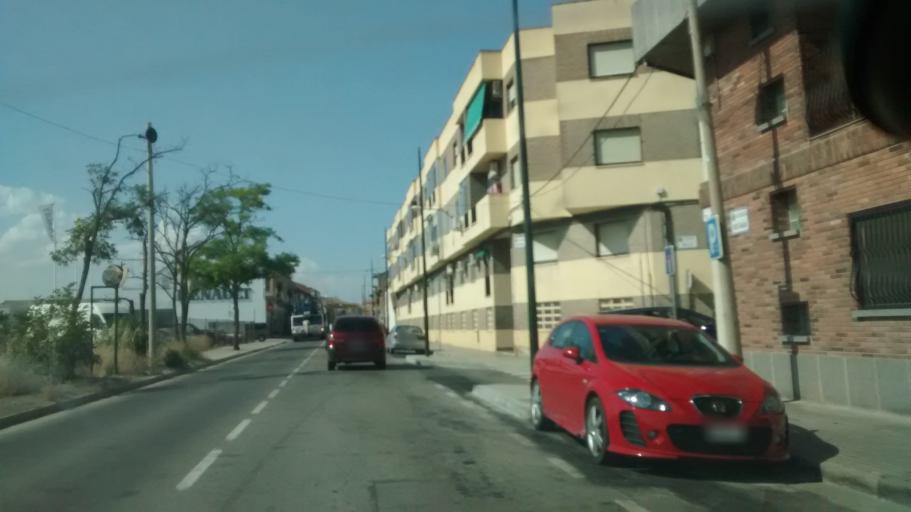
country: ES
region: Aragon
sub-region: Provincia de Zaragoza
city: Zaragoza
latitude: 41.6853
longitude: -0.8288
